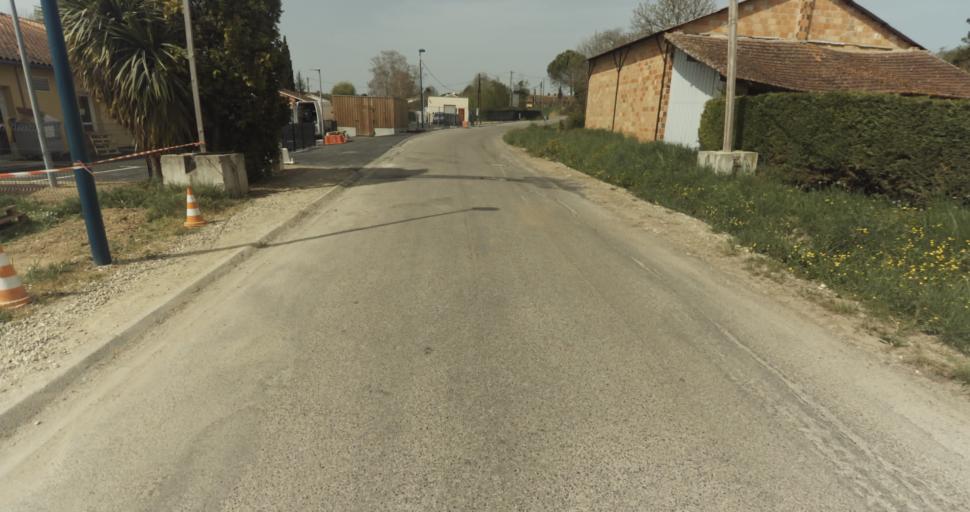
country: FR
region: Midi-Pyrenees
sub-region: Departement du Tarn-et-Garonne
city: Moissac
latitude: 44.1171
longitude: 1.1091
